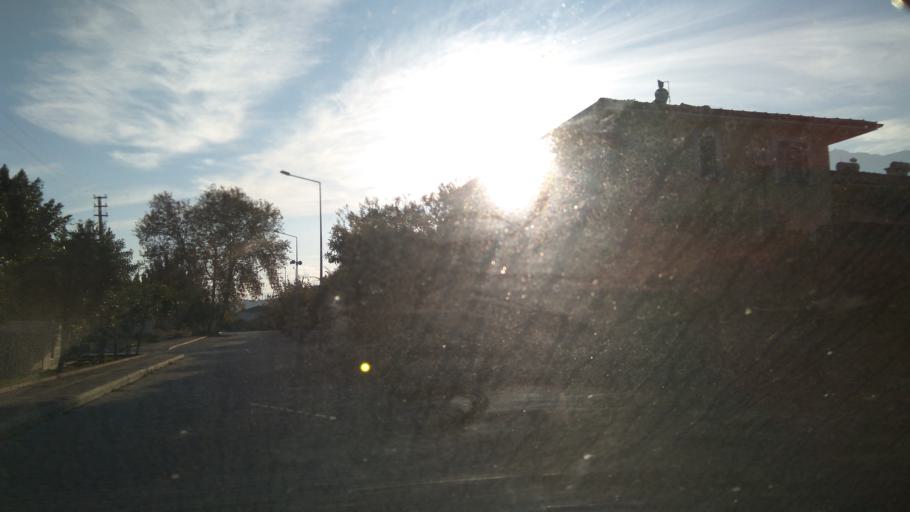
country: TR
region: Antalya
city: Kemer
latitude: 36.5681
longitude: 30.5611
